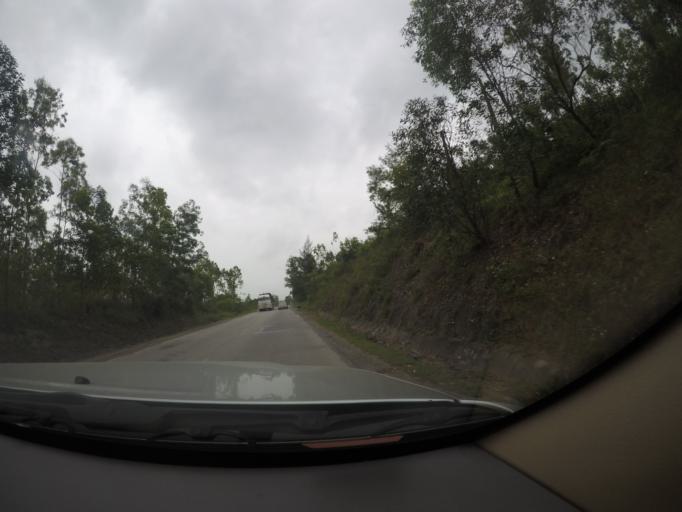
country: VN
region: Quang Binh
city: Quan Hau
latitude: 17.3199
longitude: 106.6253
